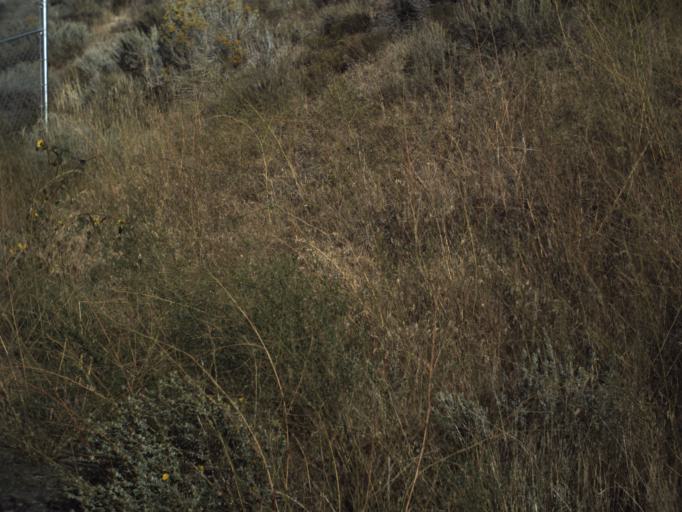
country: US
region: Utah
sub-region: Utah County
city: Santaquin
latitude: 39.9495
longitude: -111.8016
